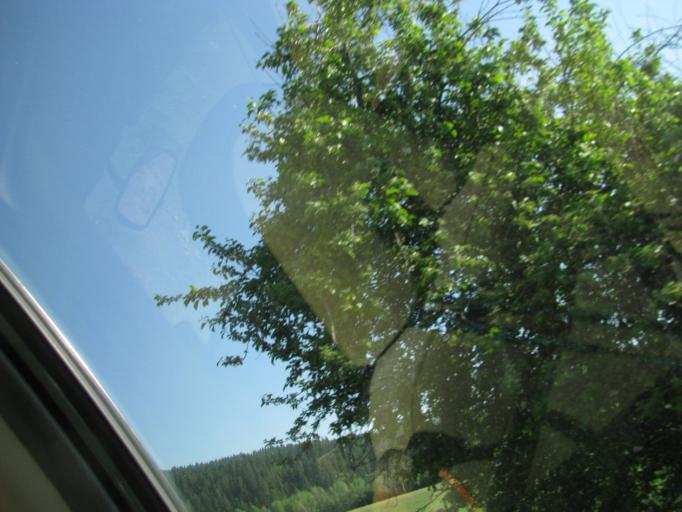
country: US
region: Washington
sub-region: Spokane County
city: Liberty Lake
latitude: 47.6169
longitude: -117.1105
